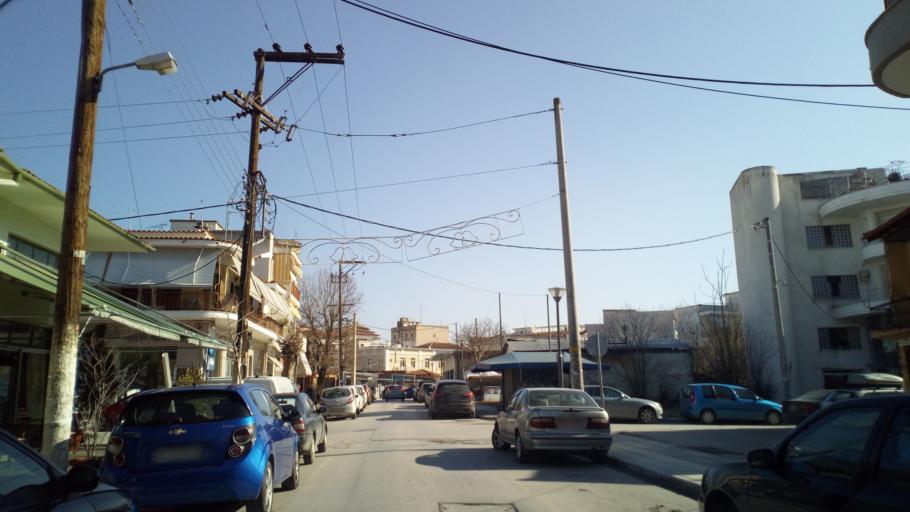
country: GR
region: Central Macedonia
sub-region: Nomos Thessalonikis
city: Lagkadas
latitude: 40.7491
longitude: 23.0664
